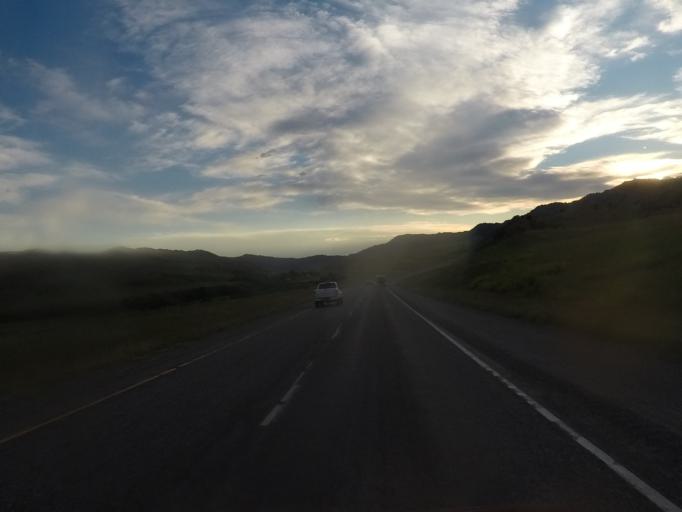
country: US
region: Montana
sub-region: Park County
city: Livingston
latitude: 45.6630
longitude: -110.6734
